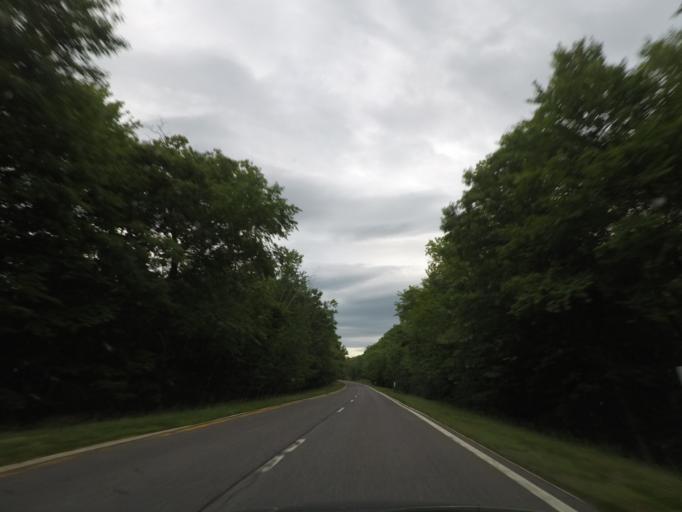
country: US
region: New York
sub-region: Dutchess County
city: Pine Plains
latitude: 42.0534
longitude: -73.7308
